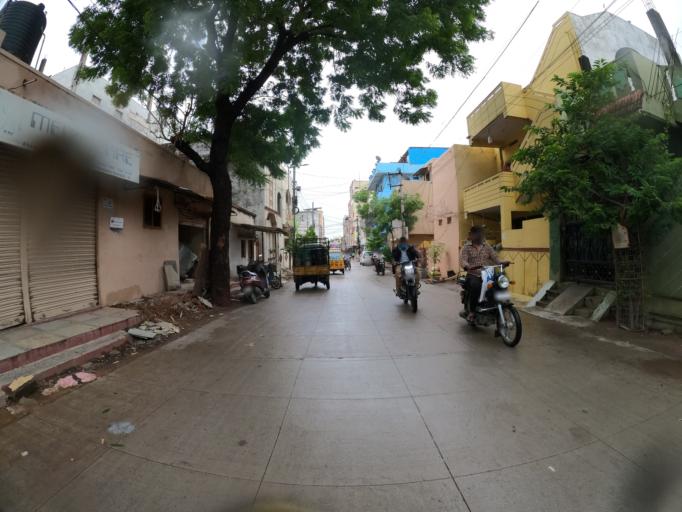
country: IN
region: Telangana
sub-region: Rangareddi
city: Kukatpalli
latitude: 17.4549
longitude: 78.4118
